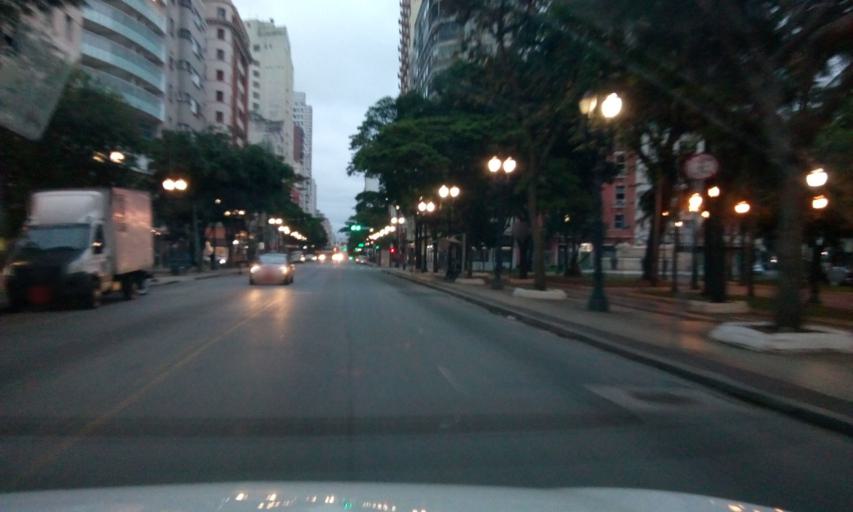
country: BR
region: Sao Paulo
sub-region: Sao Paulo
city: Sao Paulo
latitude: -23.5410
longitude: -46.6425
